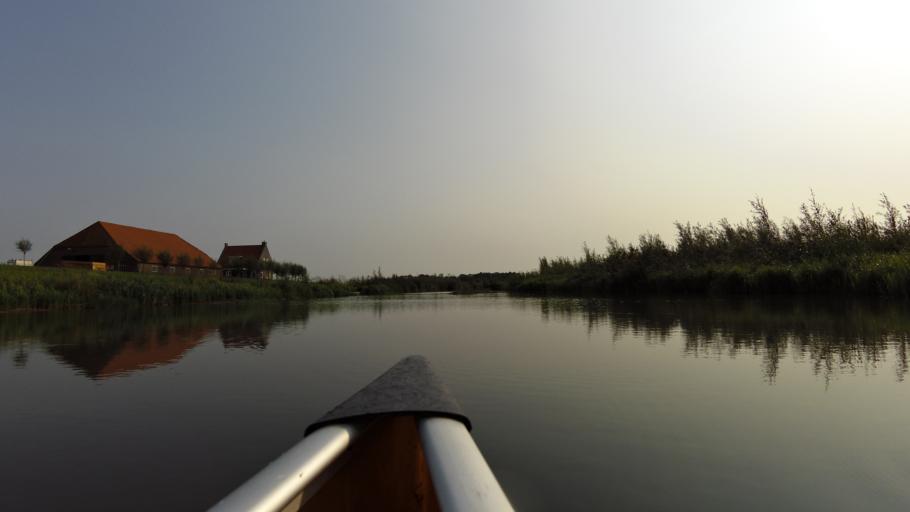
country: NL
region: South Holland
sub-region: Gemeente Sliedrecht
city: Sliedrecht
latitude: 51.7888
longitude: 4.8025
